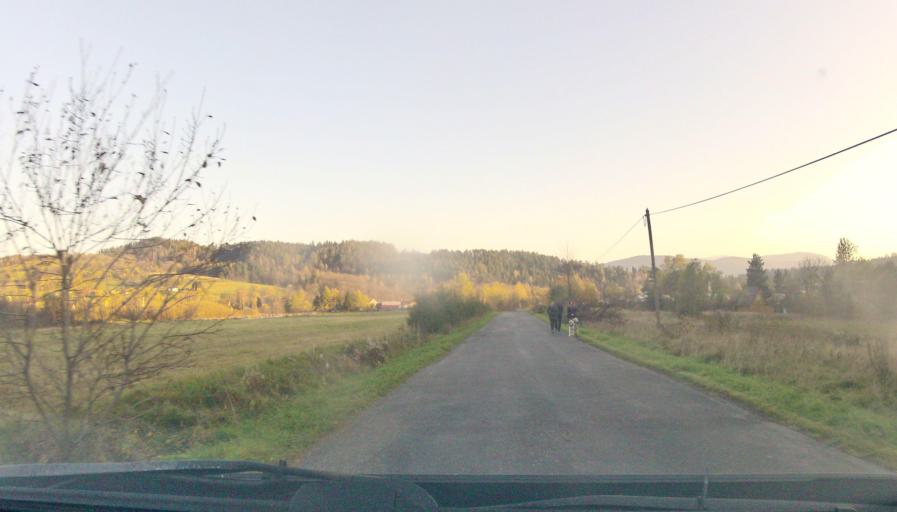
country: PL
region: Lesser Poland Voivodeship
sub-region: Powiat suski
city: Krzeszow
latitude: 49.7512
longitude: 19.4627
